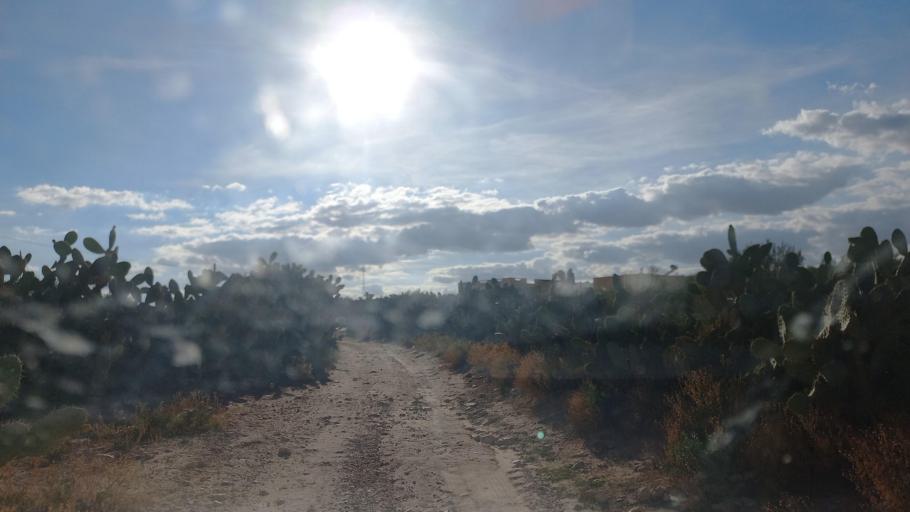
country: TN
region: Al Qasrayn
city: Sbiba
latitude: 35.3820
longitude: 9.0253
